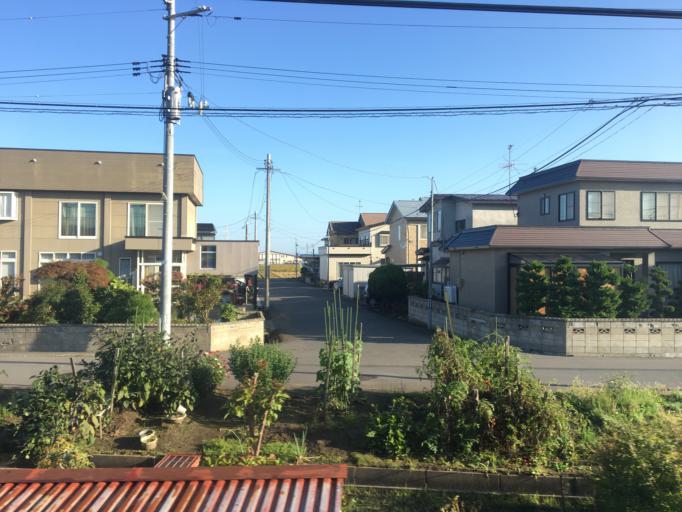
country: JP
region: Aomori
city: Hirosaki
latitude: 40.5877
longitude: 140.5181
